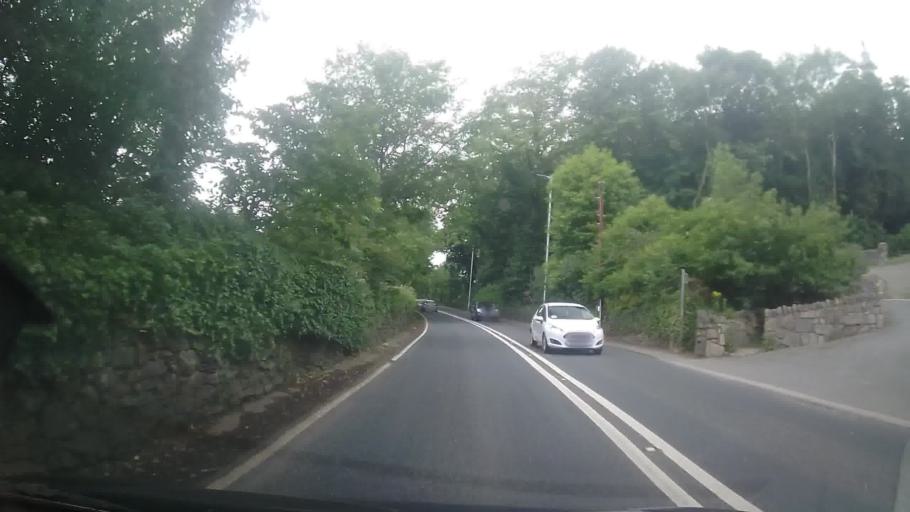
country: GB
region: Wales
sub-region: Anglesey
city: Llanfairpwllgwyngyll
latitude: 53.2201
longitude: -4.1954
